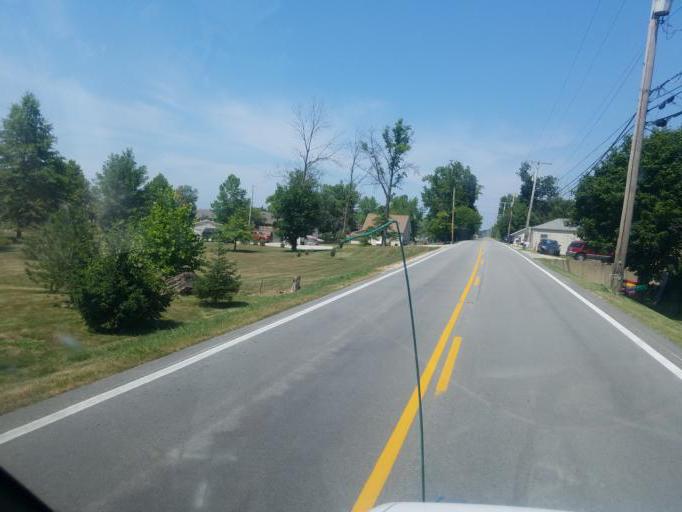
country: US
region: Ohio
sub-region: Auglaize County
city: Saint Marys
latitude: 40.5147
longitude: -84.4243
